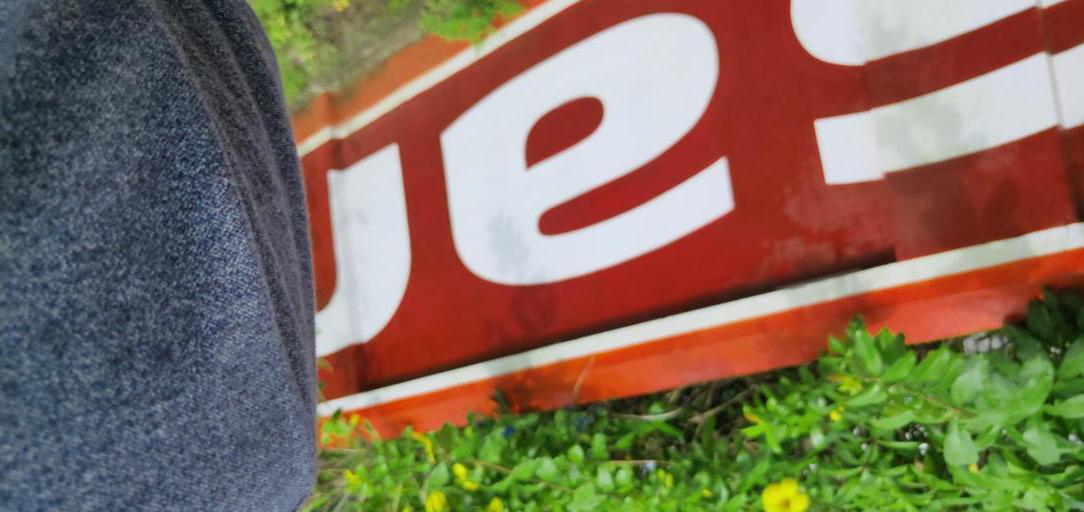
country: IN
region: Kerala
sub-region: Alappuzha
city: Kayankulam
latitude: 9.2277
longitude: 76.4584
